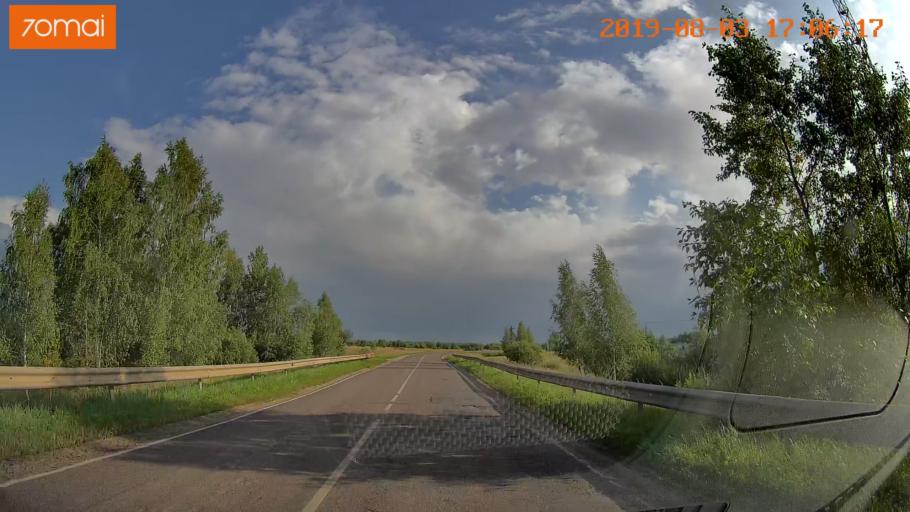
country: RU
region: Moskovskaya
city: Troitskoye
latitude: 55.3101
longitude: 38.5513
